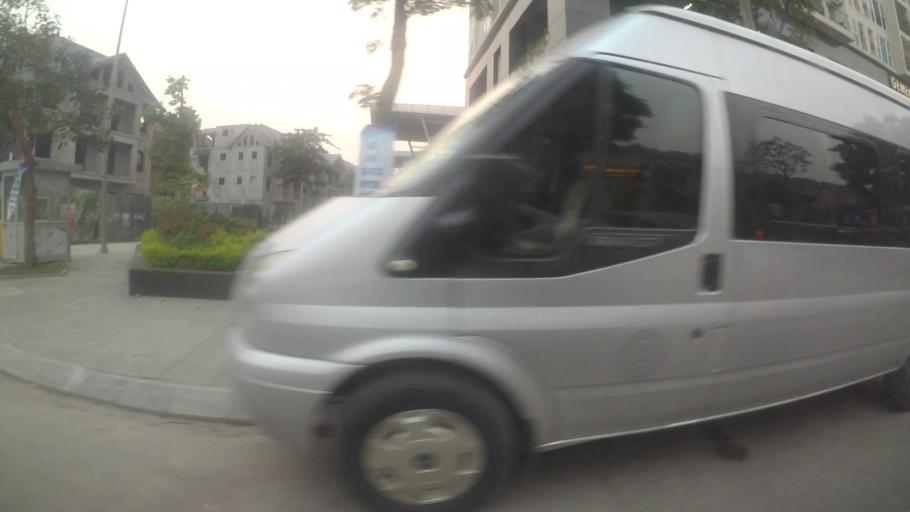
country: VN
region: Ha Noi
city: Cau Dien
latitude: 21.0029
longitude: 105.7326
